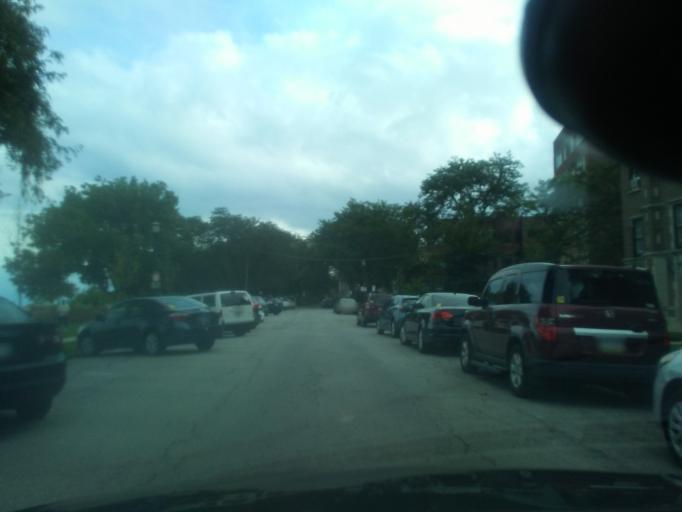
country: US
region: Illinois
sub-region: Cook County
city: Evanston
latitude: 42.0286
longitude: -87.6689
